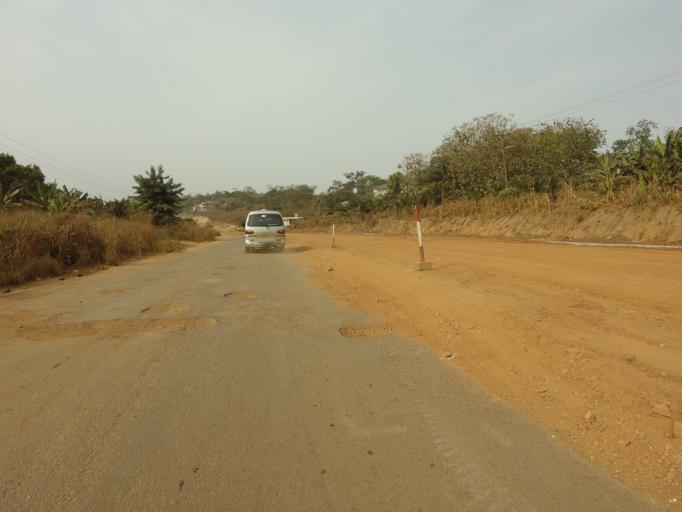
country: GH
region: Volta
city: Ho
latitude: 6.5924
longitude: 0.4341
